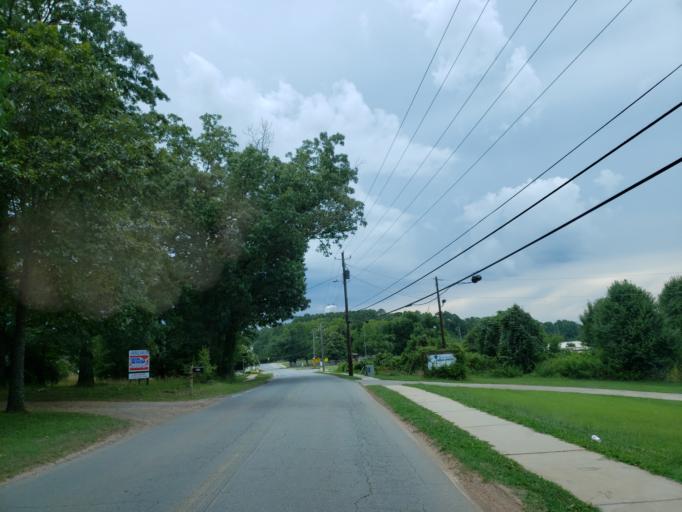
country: US
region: Georgia
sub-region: Cherokee County
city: Woodstock
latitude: 34.1070
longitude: -84.5212
